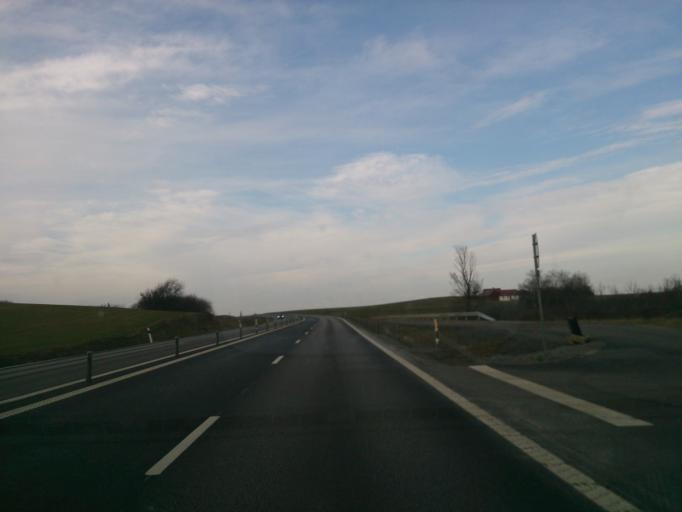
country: SE
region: Skane
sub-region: Svedala Kommun
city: Klagerup
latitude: 55.5677
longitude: 13.2559
